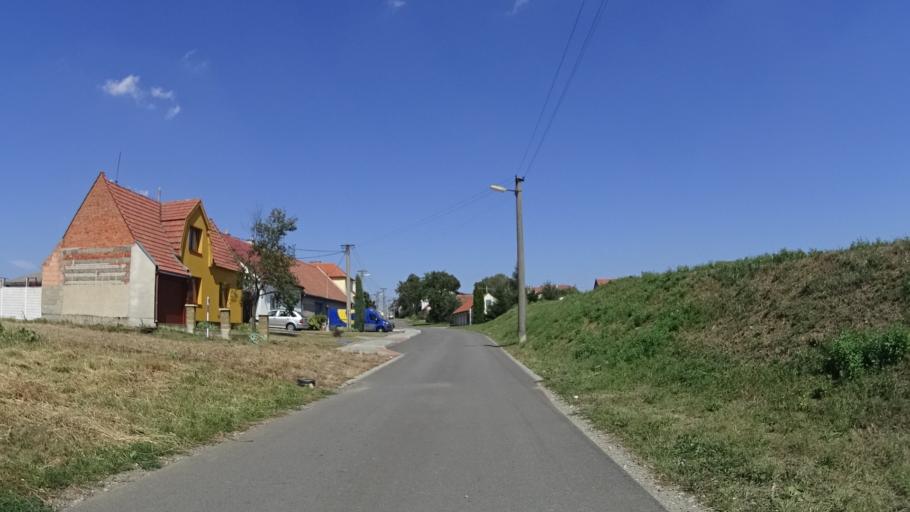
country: CZ
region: South Moravian
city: Vnorovy
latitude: 48.9210
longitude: 17.3366
